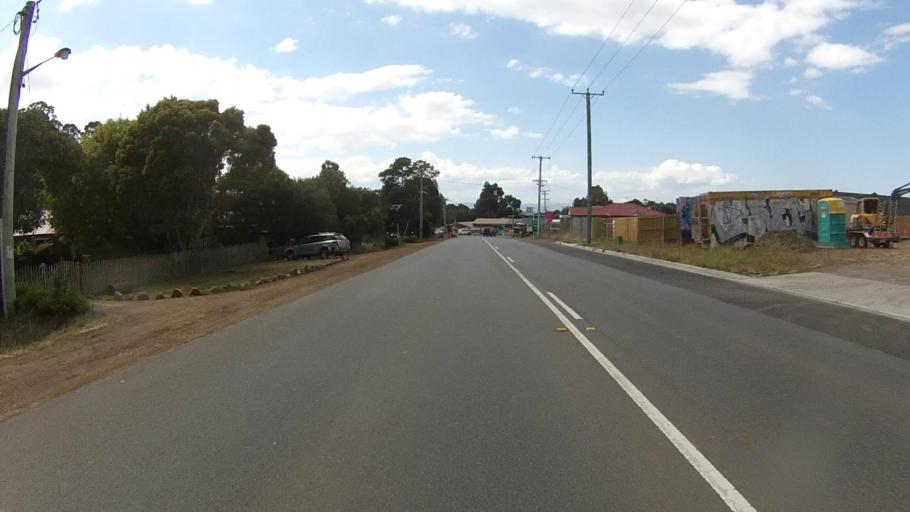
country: AU
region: Tasmania
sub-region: Clarence
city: Cambridge
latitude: -42.8375
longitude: 147.4394
